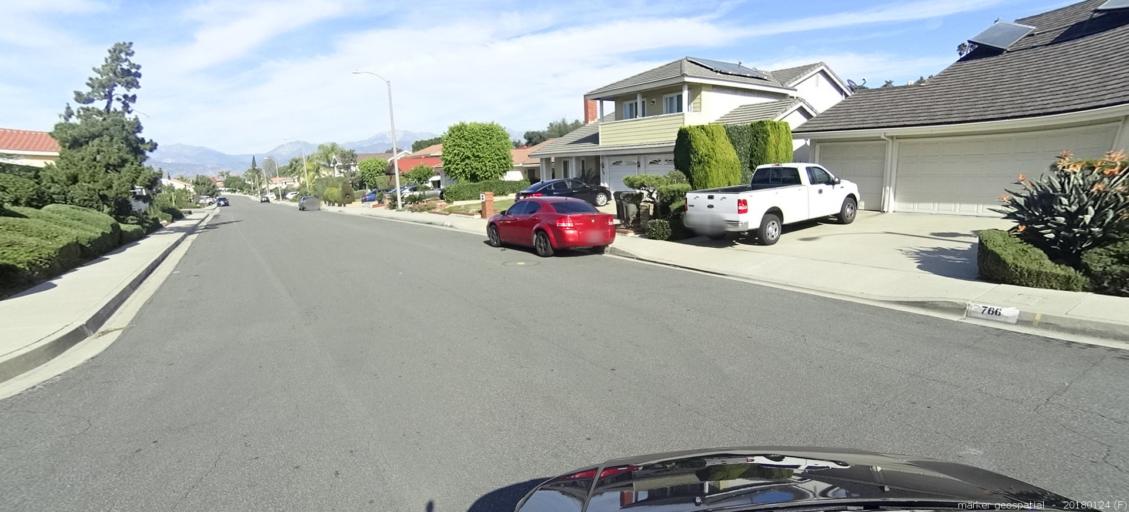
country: US
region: California
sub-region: Los Angeles County
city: Diamond Bar
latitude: 34.0106
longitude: -117.8084
